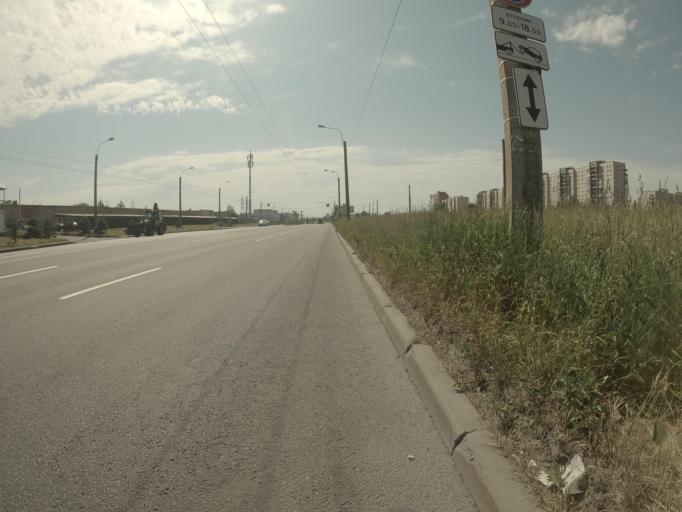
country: RU
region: St.-Petersburg
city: Krasnogvargeisky
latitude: 59.9404
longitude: 30.5042
